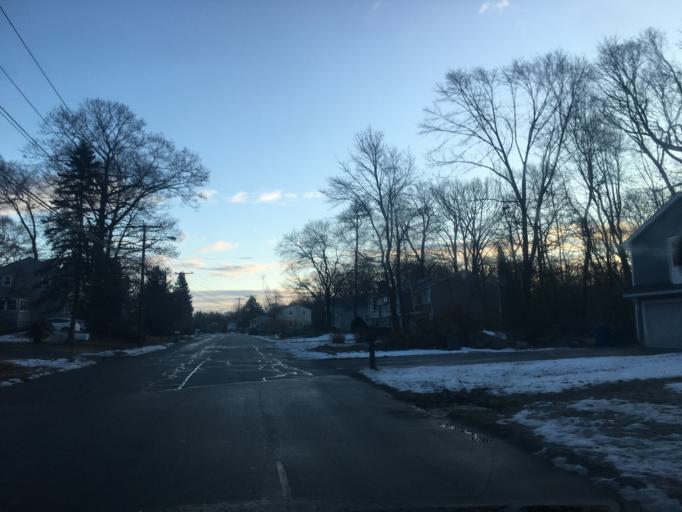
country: US
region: Massachusetts
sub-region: Middlesex County
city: Billerica
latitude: 42.5468
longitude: -71.2688
